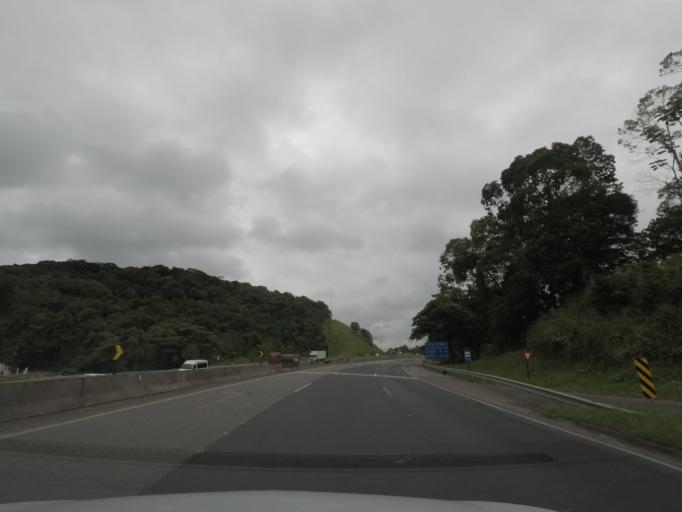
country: BR
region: Sao Paulo
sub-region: Juquia
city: Juquia
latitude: -24.3872
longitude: -47.7172
